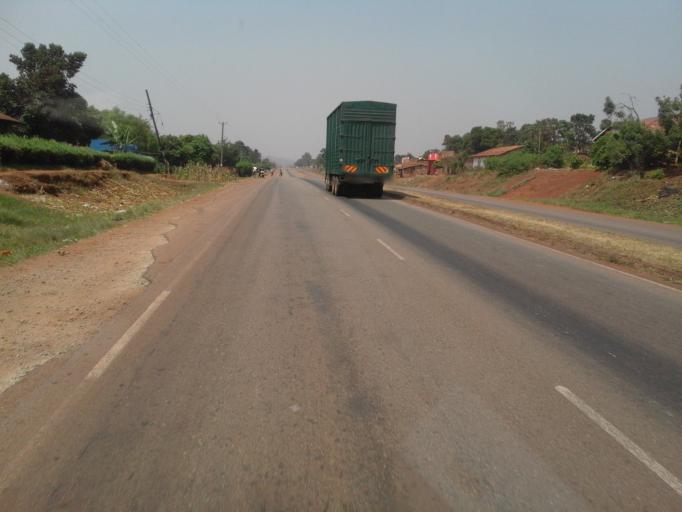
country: UG
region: Eastern Region
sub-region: Jinja District
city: Bugembe
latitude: 0.4732
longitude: 33.2571
